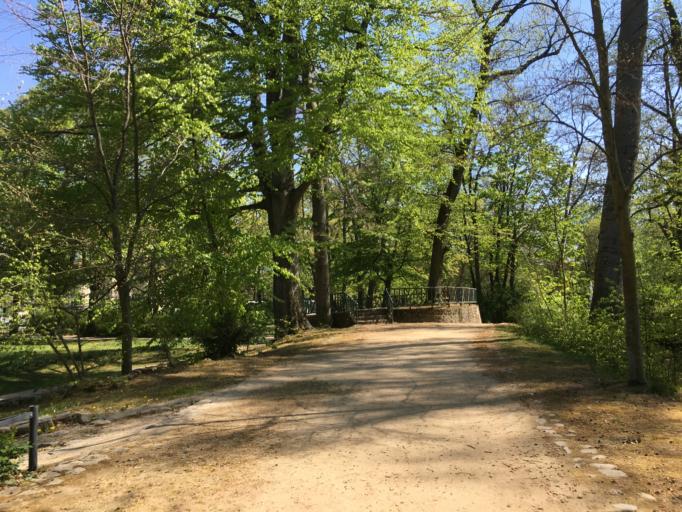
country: DE
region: Brandenburg
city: Bernau bei Berlin
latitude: 52.6814
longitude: 13.5891
